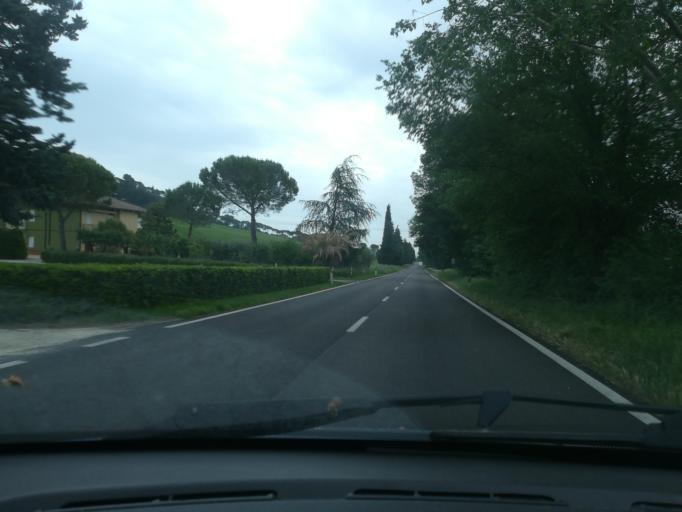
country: IT
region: The Marches
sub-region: Provincia di Macerata
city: Treia
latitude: 43.2731
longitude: 13.2864
